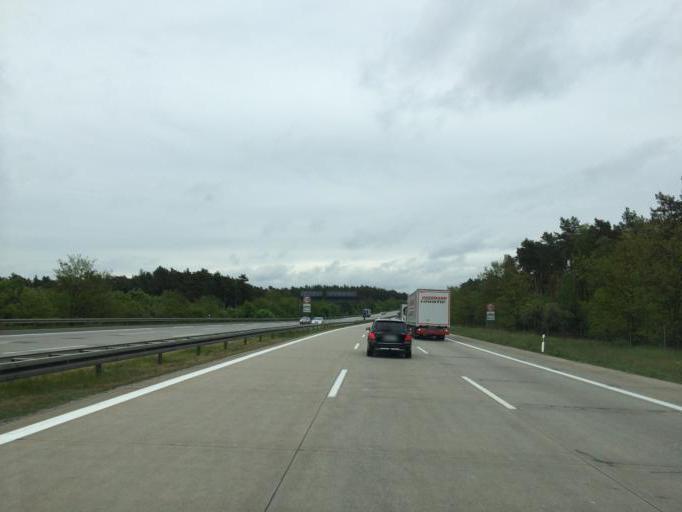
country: DE
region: Brandenburg
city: Golzow
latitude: 52.3500
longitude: 12.6030
